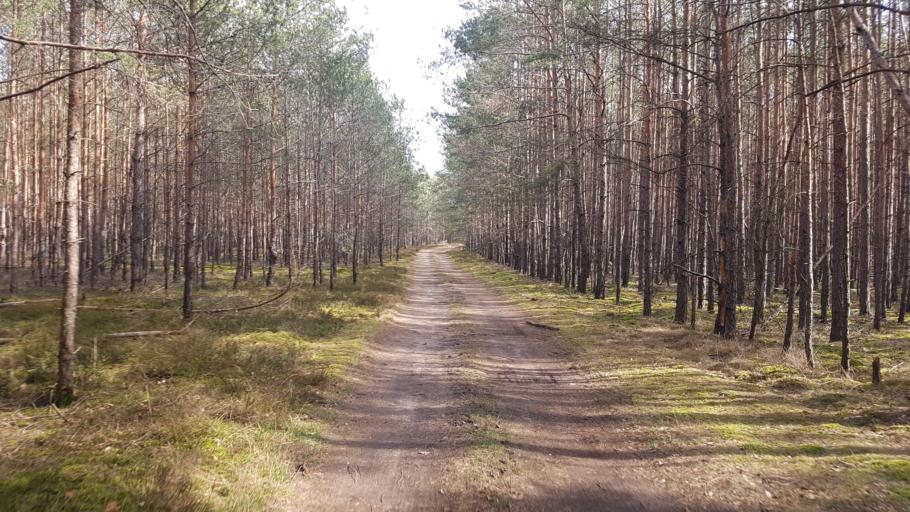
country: DE
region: Brandenburg
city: Doberlug-Kirchhain
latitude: 51.6222
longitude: 13.6204
